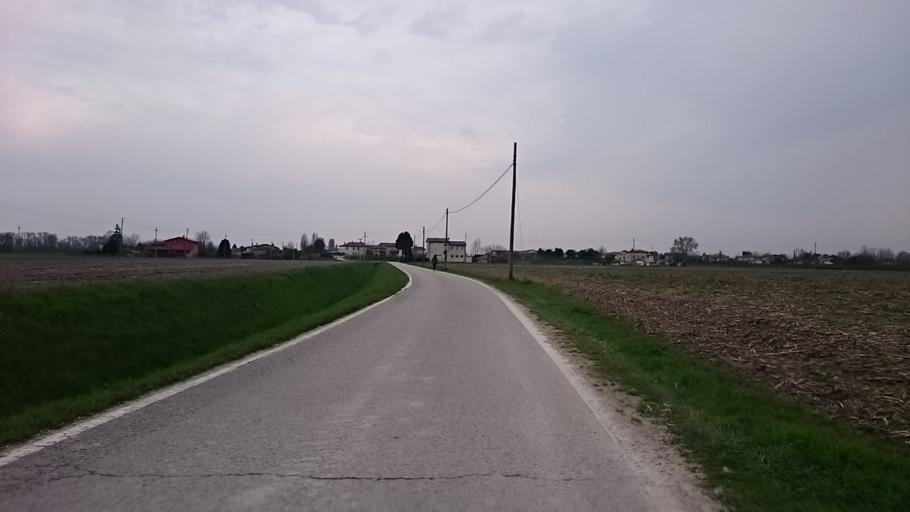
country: IT
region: Veneto
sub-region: Provincia di Padova
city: Tremignon
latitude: 45.5272
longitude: 11.8083
